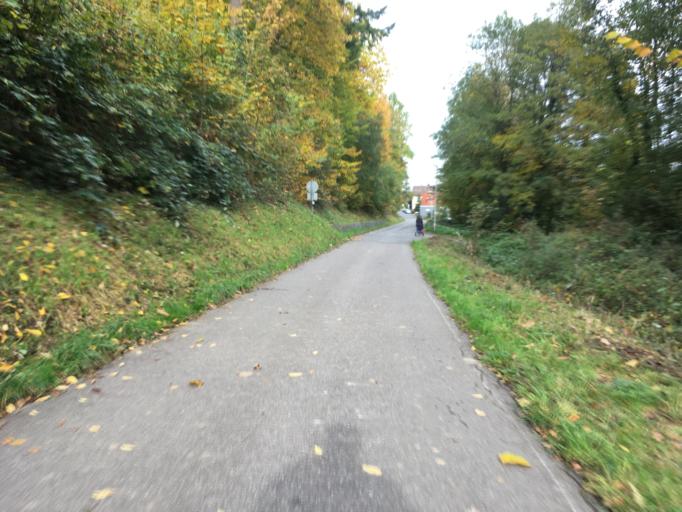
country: DE
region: Baden-Wuerttemberg
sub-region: Karlsruhe Region
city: Adelsheim
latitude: 49.3971
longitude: 9.3916
